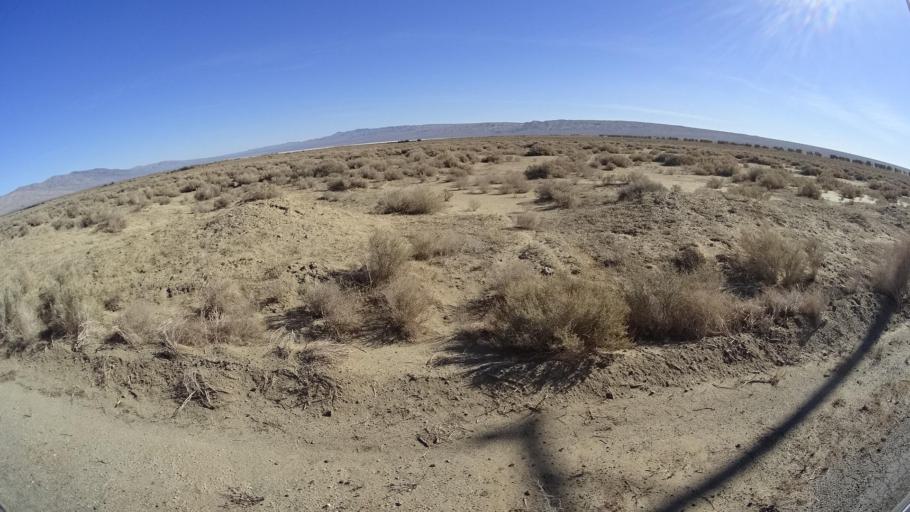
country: US
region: California
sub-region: Kern County
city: California City
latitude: 35.2926
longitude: -117.9681
